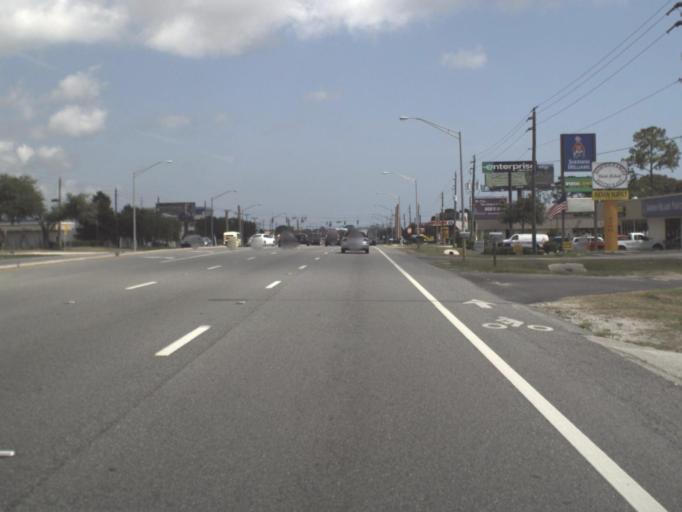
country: US
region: Florida
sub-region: Saint Johns County
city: Saint Augustine South
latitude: 29.8584
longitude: -81.3228
